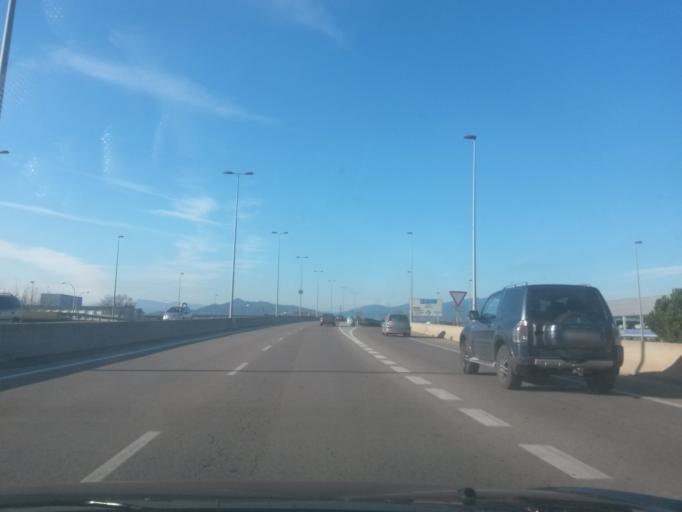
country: ES
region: Catalonia
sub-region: Provincia de Girona
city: Salt
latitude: 41.9586
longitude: 2.8046
